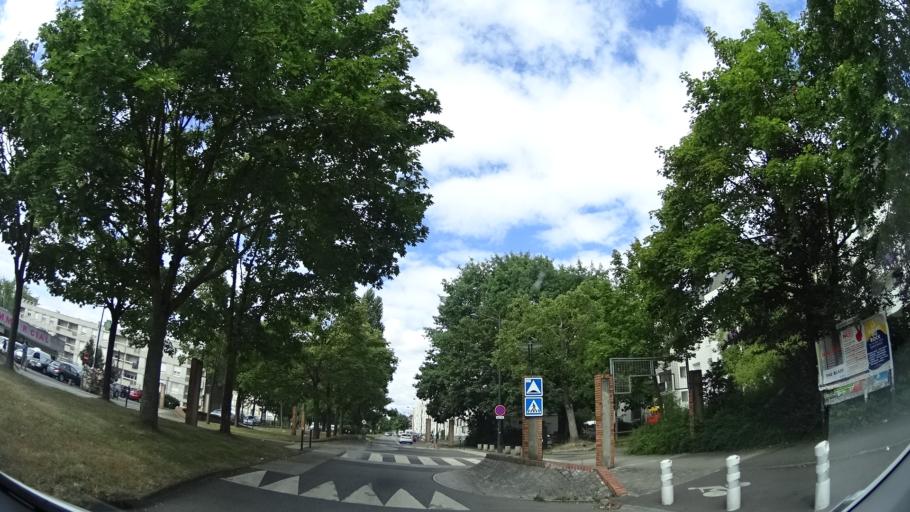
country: FR
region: Brittany
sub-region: Departement d'Ille-et-Vilaine
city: Rennes
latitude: 48.0916
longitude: -1.6518
